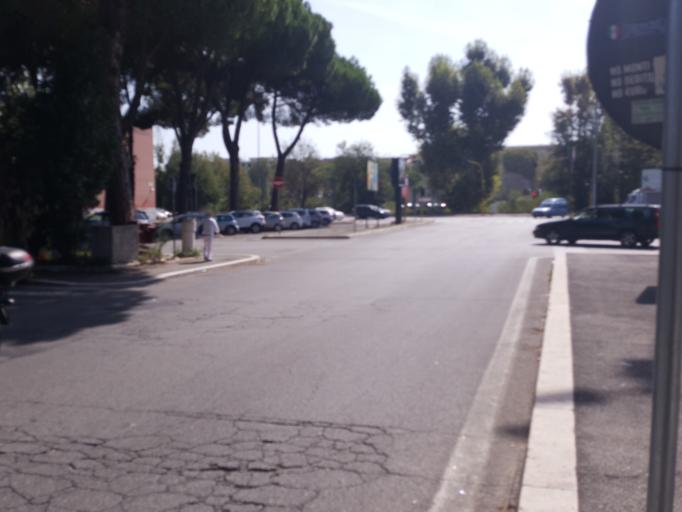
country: VA
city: Vatican City
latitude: 41.9354
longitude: 12.4625
